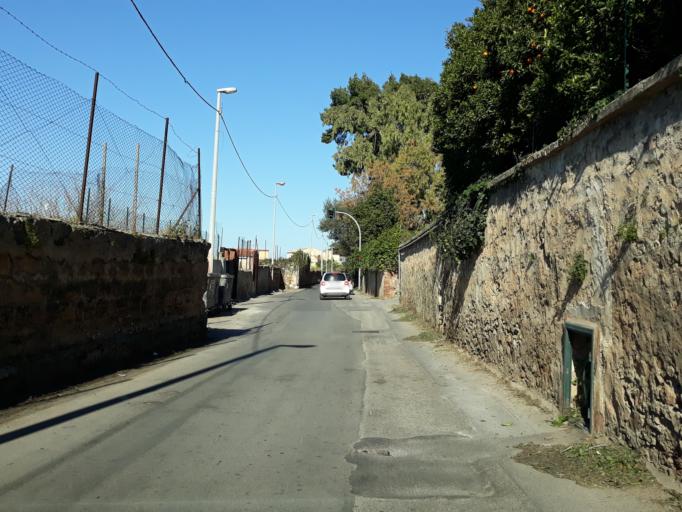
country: IT
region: Sicily
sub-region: Palermo
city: Ciaculli
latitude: 38.0819
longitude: 13.3750
